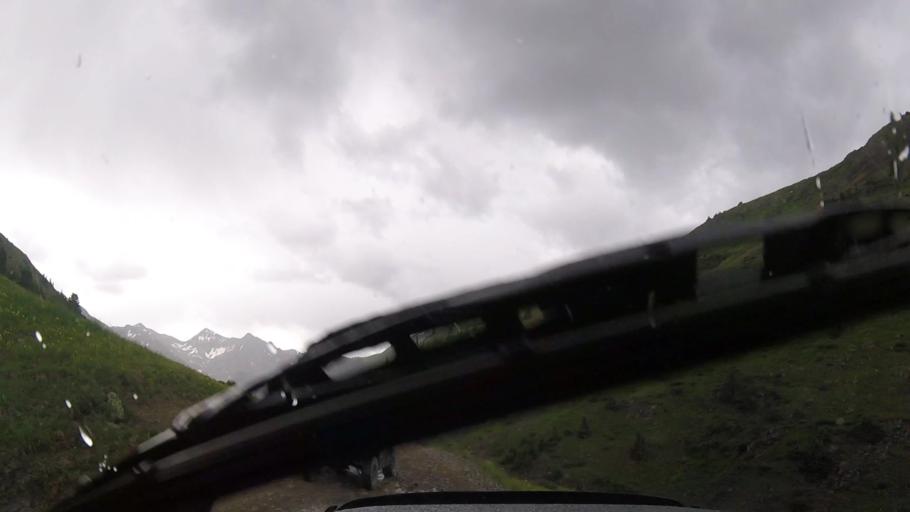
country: US
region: Colorado
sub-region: Ouray County
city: Ouray
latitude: 37.9398
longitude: -107.5735
